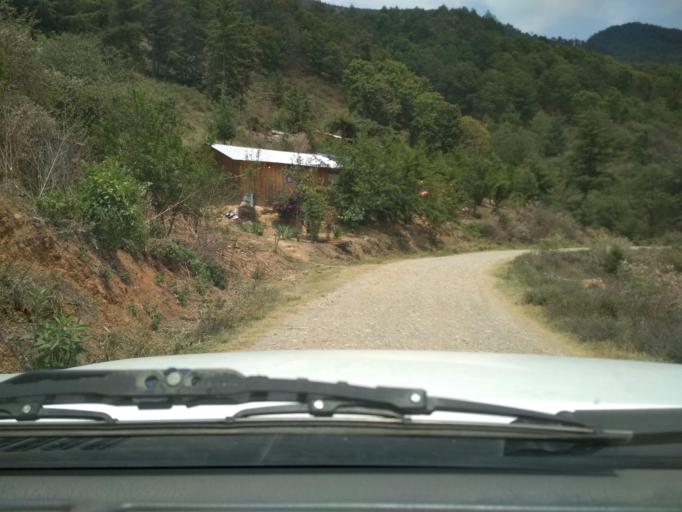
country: MX
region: Veracruz
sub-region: Acultzingo
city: Acatla
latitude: 18.7475
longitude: -97.1894
